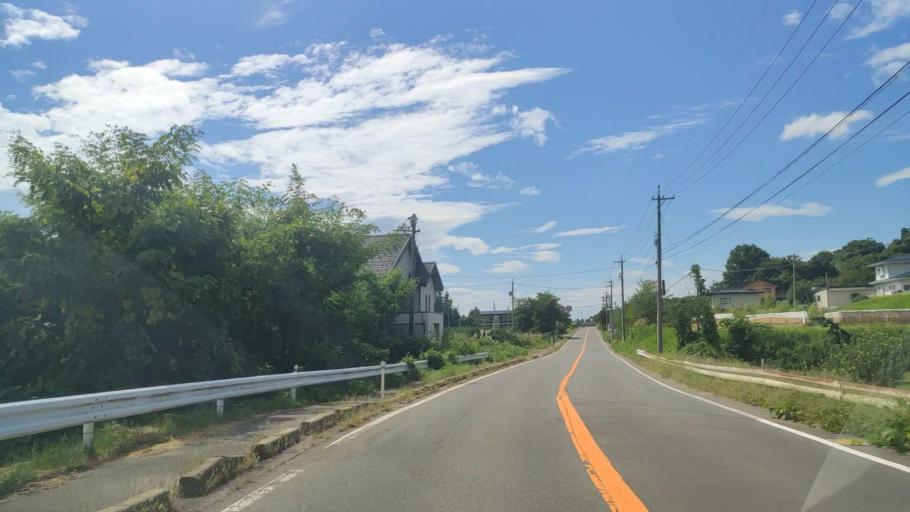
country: JP
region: Nagano
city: Nakano
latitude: 36.7486
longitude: 138.3146
